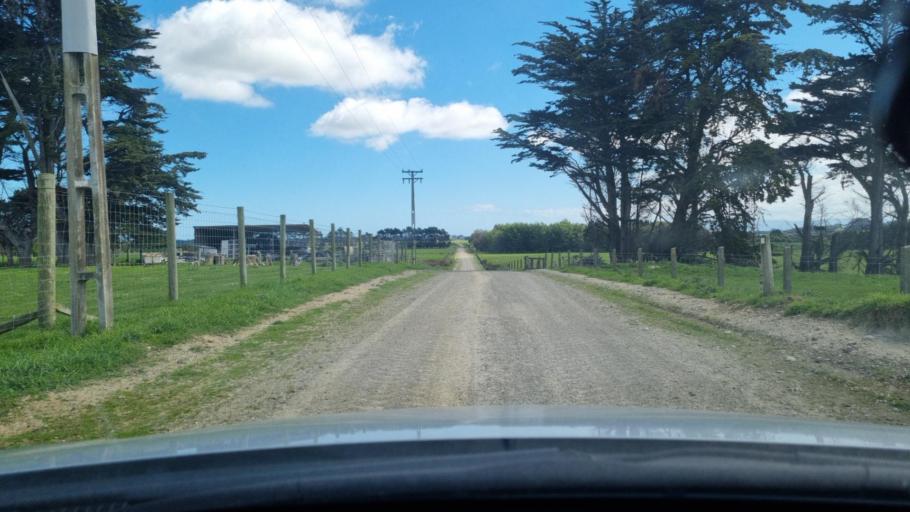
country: NZ
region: Southland
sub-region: Invercargill City
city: Invercargill
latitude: -46.3510
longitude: 168.3066
